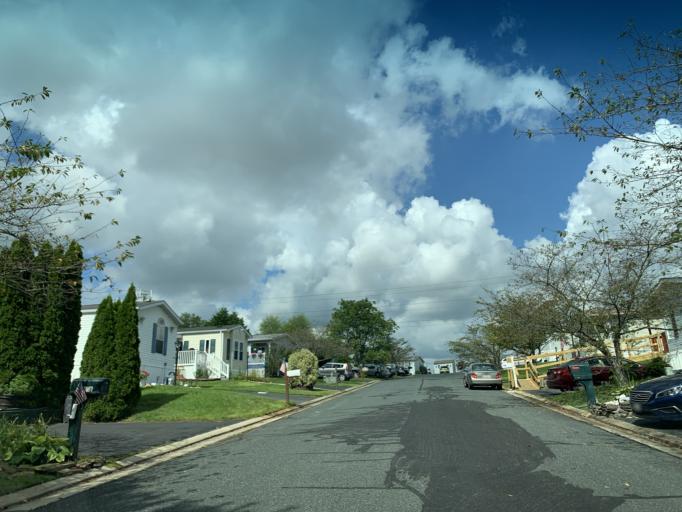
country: US
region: Maryland
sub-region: Baltimore County
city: White Marsh
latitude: 39.3594
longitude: -76.4382
